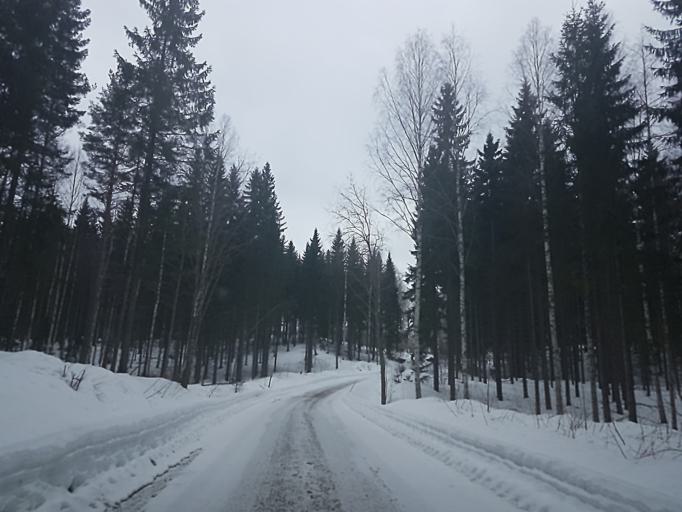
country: FI
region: Northern Savo
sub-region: Koillis-Savo
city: Kaavi
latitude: 62.9780
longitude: 28.7560
